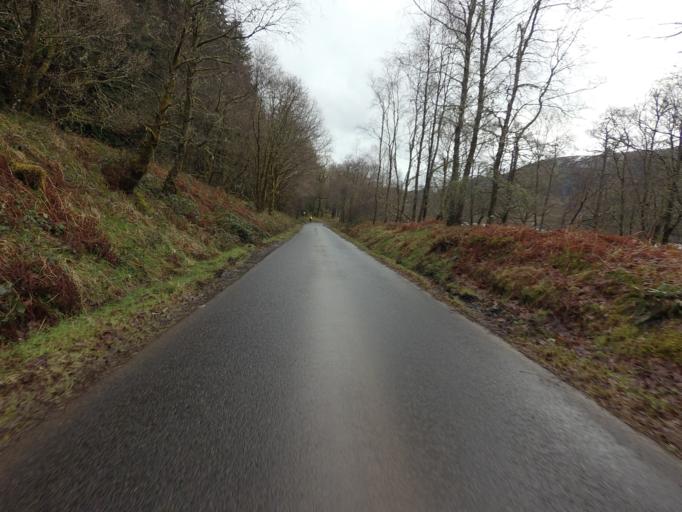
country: GB
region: Scotland
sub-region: West Dunbartonshire
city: Balloch
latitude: 56.2240
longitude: -4.5520
